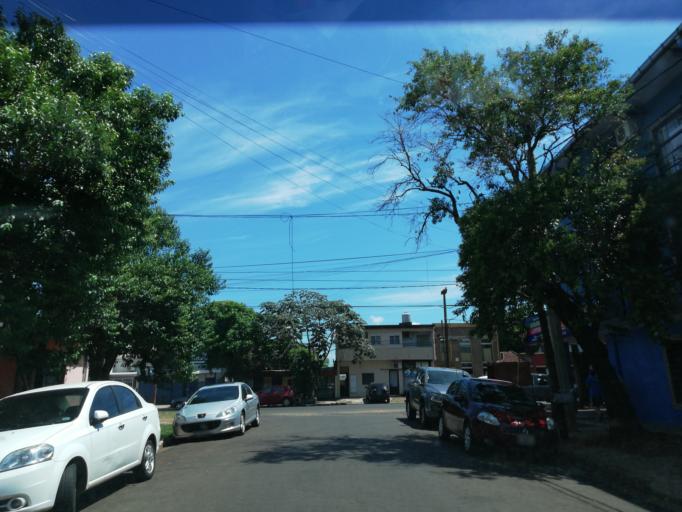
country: AR
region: Misiones
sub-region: Departamento de Capital
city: Posadas
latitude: -27.3736
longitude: -55.9082
